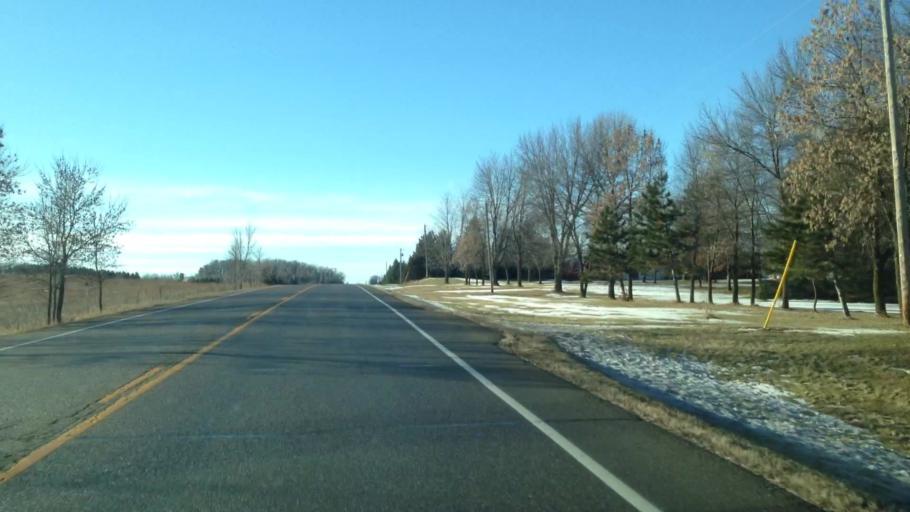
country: US
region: Minnesota
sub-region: Dakota County
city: Farmington
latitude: 44.5992
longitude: -93.0102
